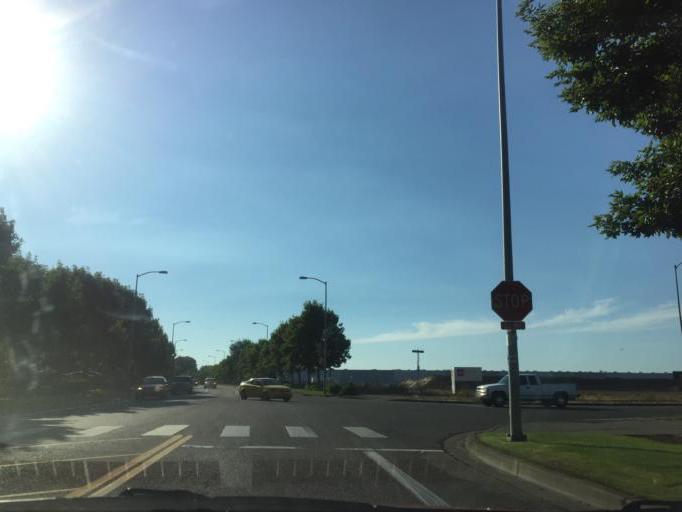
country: US
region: Oregon
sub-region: Multnomah County
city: Lents
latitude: 45.5690
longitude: -122.5600
